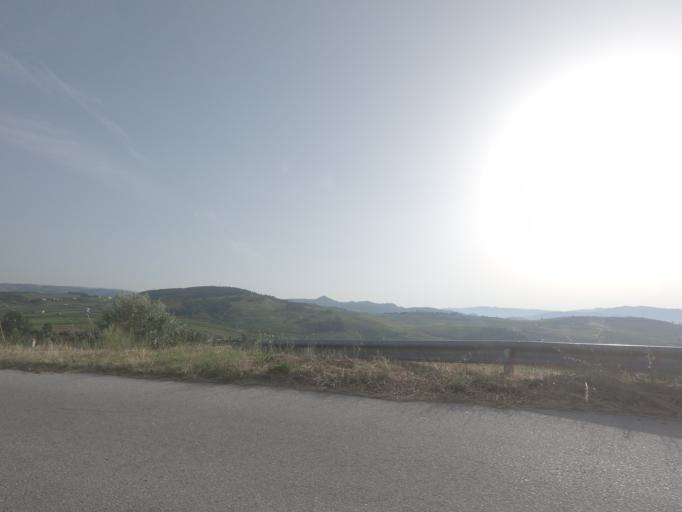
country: PT
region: Viseu
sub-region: Sao Joao da Pesqueira
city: Sao Joao da Pesqueira
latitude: 41.2345
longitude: -7.4673
